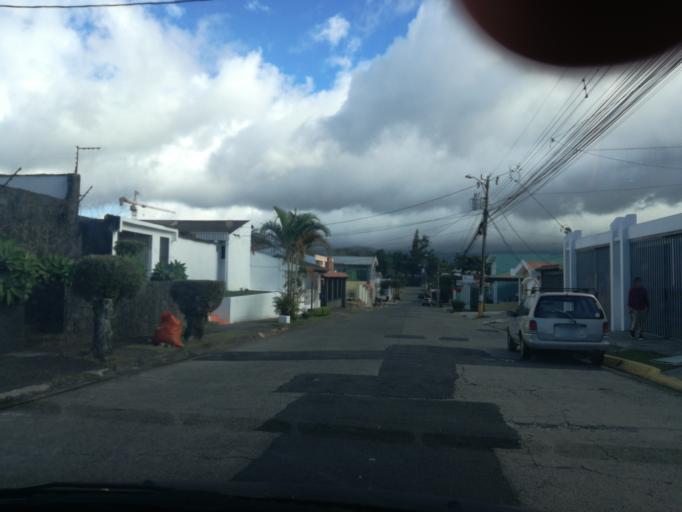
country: CR
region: San Jose
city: San Pedro
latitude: 9.9262
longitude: -84.0425
